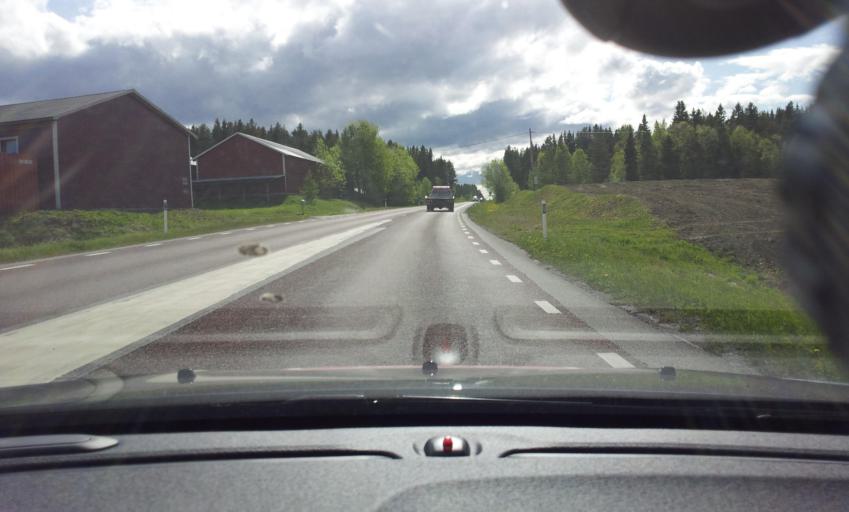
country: SE
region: Jaemtland
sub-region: OEstersunds Kommun
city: Brunflo
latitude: 63.0172
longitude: 14.7326
